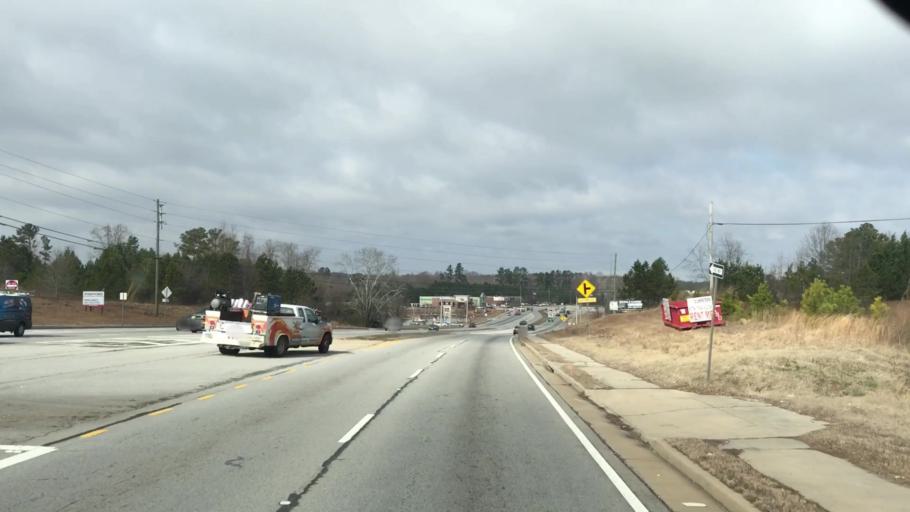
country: US
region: Georgia
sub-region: Hall County
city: Oakwood
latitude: 34.1909
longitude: -83.8574
